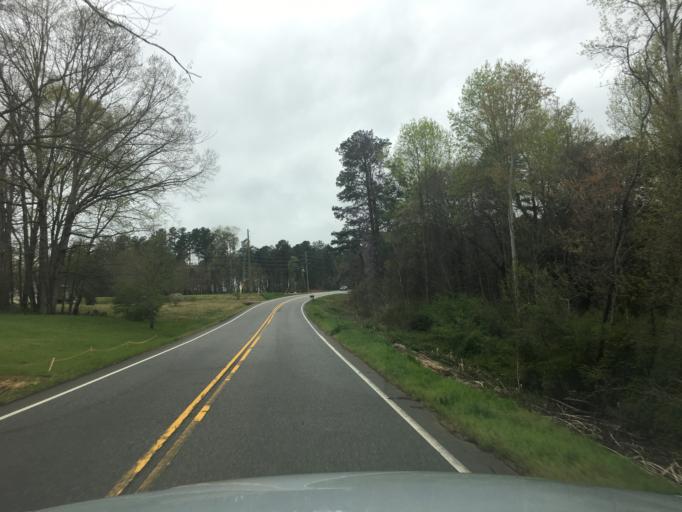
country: US
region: South Carolina
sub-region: Spartanburg County
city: Fairforest
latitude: 34.9706
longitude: -82.0483
